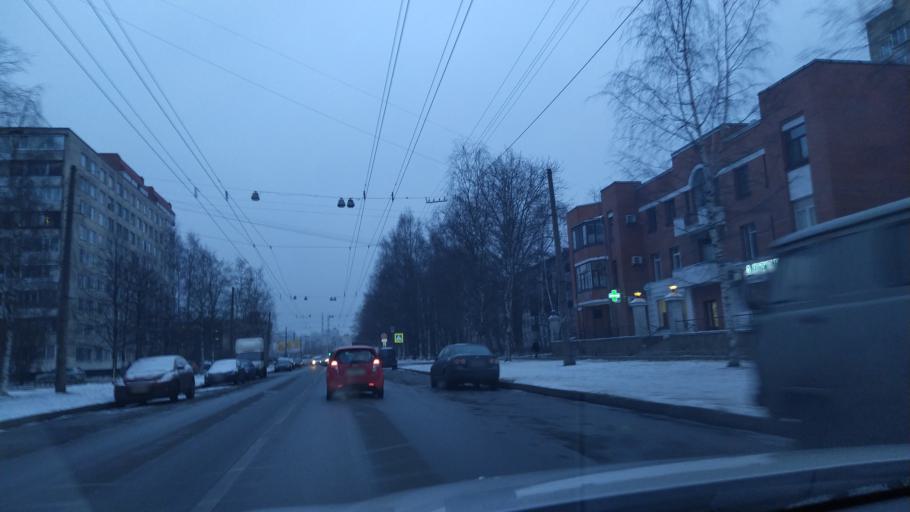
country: RU
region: Leningrad
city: Akademicheskoe
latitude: 60.0164
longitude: 30.4144
